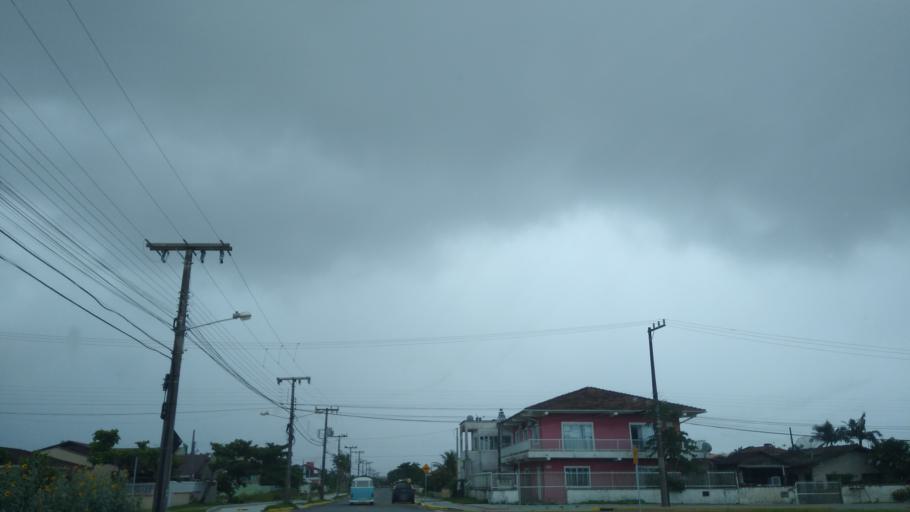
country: BR
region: Santa Catarina
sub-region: Sao Francisco Do Sul
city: Sao Francisco do Sul
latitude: -26.2376
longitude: -48.5115
